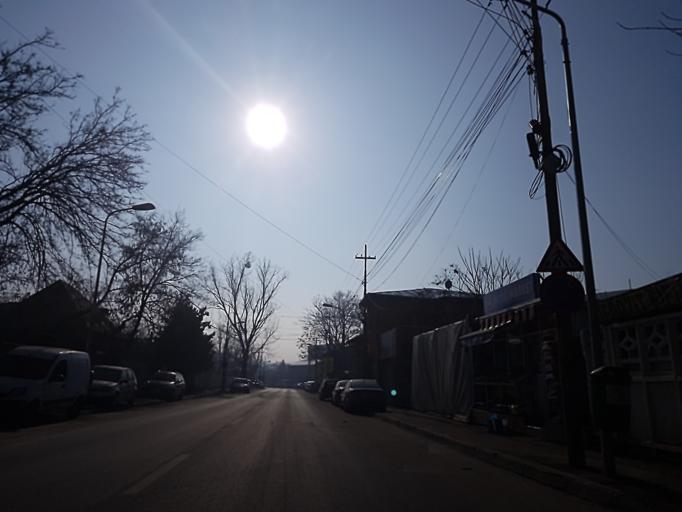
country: RO
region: Bucuresti
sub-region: Municipiul Bucuresti
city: Bucuresti
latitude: 44.4141
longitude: 26.0919
